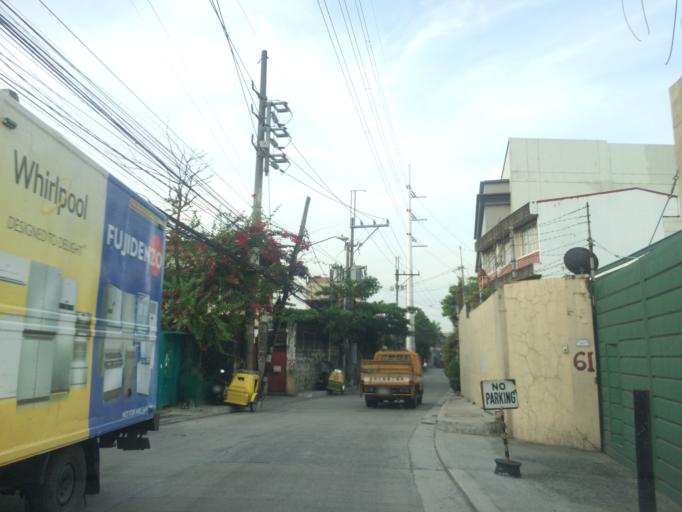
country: PH
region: Calabarzon
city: Del Monte
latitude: 14.6489
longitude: 121.0098
